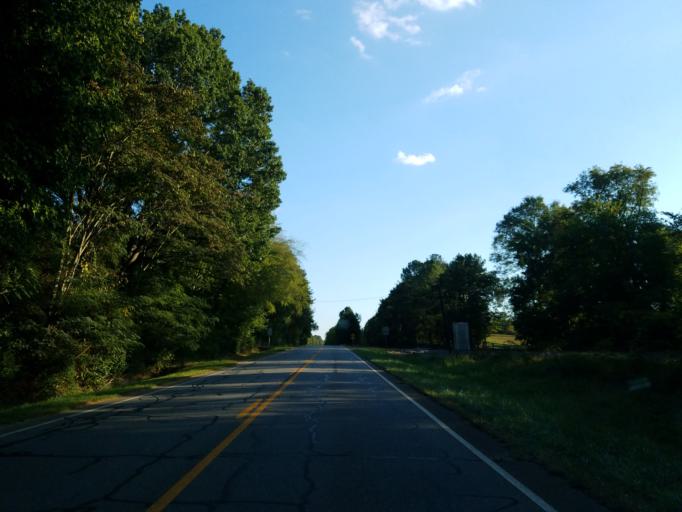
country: US
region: Georgia
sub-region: Murray County
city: Chatsworth
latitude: 34.5599
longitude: -84.7078
